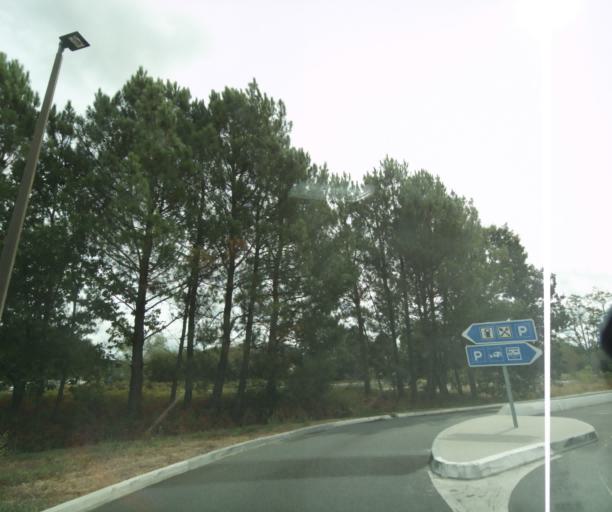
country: FR
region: Aquitaine
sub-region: Departement de la Gironde
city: Reignac
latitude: 45.1902
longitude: -0.4929
